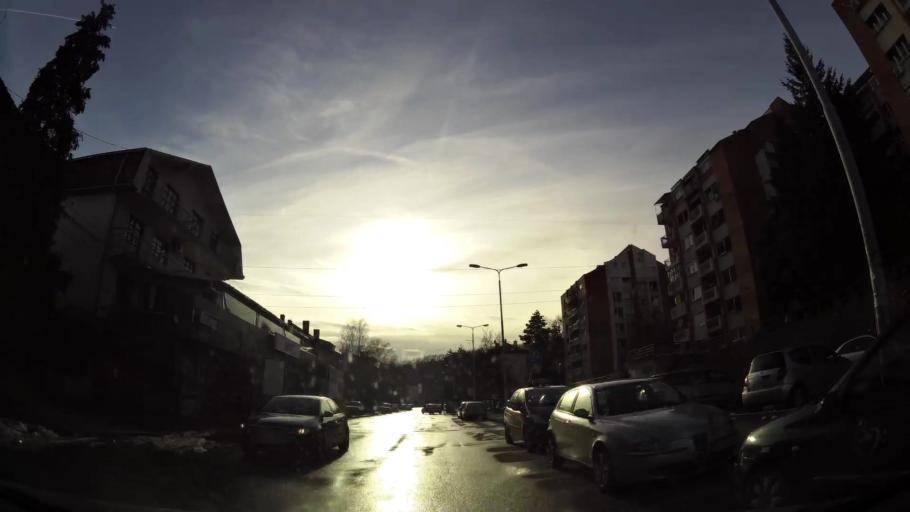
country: RS
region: Central Serbia
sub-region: Belgrade
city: Rakovica
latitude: 44.7424
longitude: 20.4342
